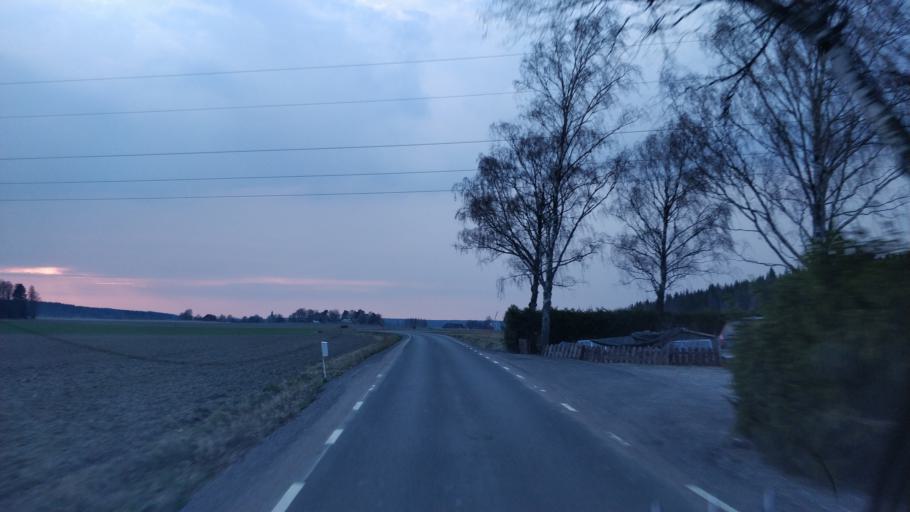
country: SE
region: Uppsala
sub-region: Enkopings Kommun
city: Orsundsbro
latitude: 59.7244
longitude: 17.2224
